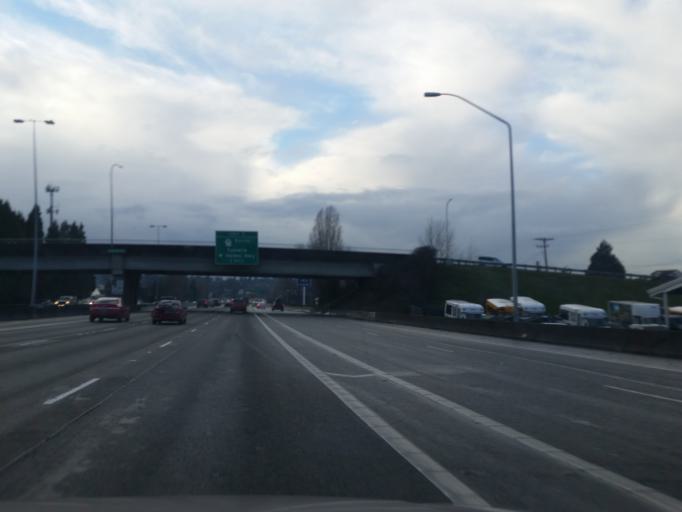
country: US
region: Washington
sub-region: King County
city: Renton
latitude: 47.4678
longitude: -122.2220
